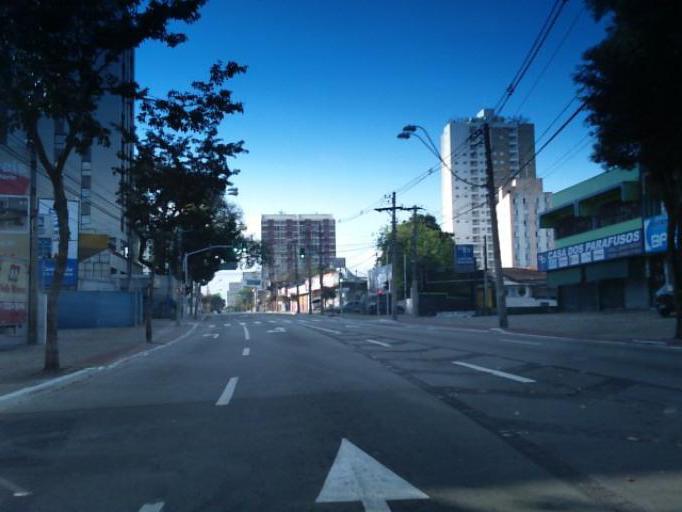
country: BR
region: Sao Paulo
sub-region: Sao Jose Dos Campos
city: Sao Jose dos Campos
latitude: -23.1926
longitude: -45.8853
